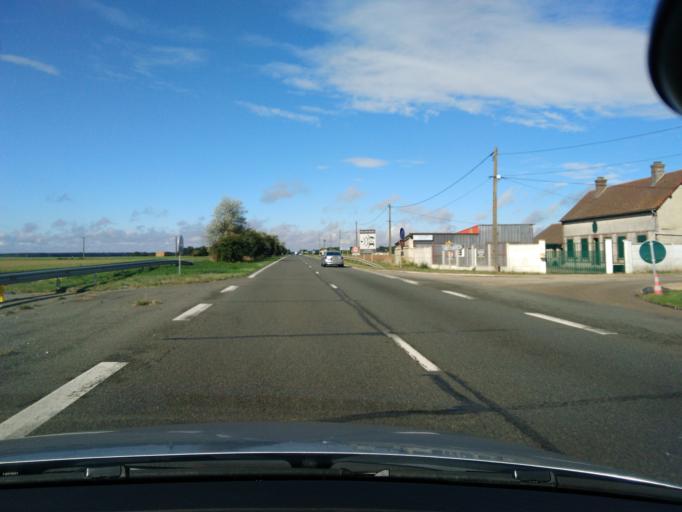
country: FR
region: Centre
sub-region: Departement d'Eure-et-Loir
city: Vert-en-Drouais
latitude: 48.7445
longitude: 1.2867
